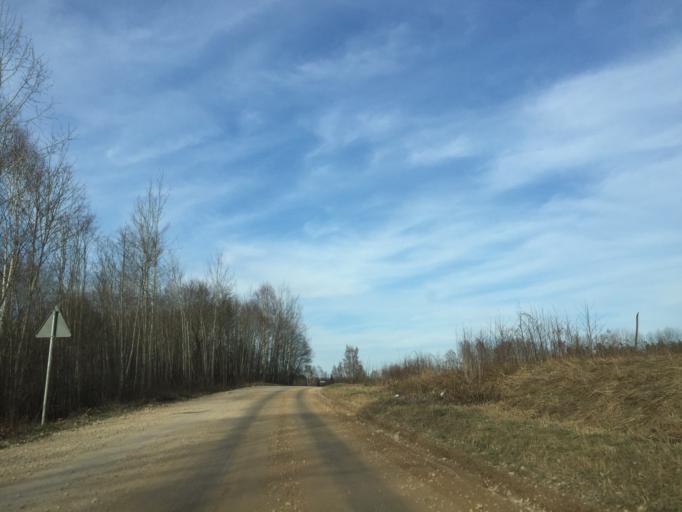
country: LV
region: Ogre
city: Ogre
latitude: 56.7847
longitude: 24.6671
